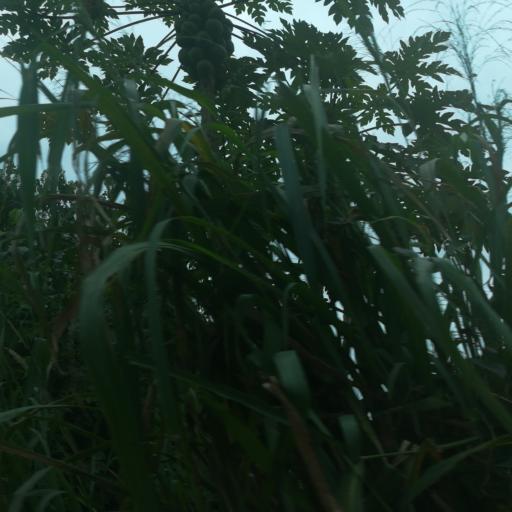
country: NG
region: Lagos
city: Ejirin
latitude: 6.6508
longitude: 3.7129
